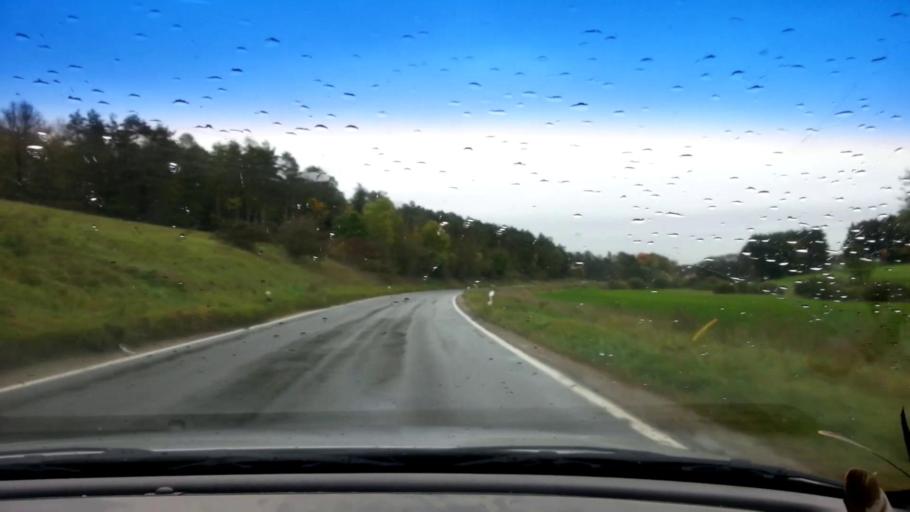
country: DE
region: Bavaria
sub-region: Upper Franconia
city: Heiligenstadt
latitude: 49.8754
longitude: 11.1441
